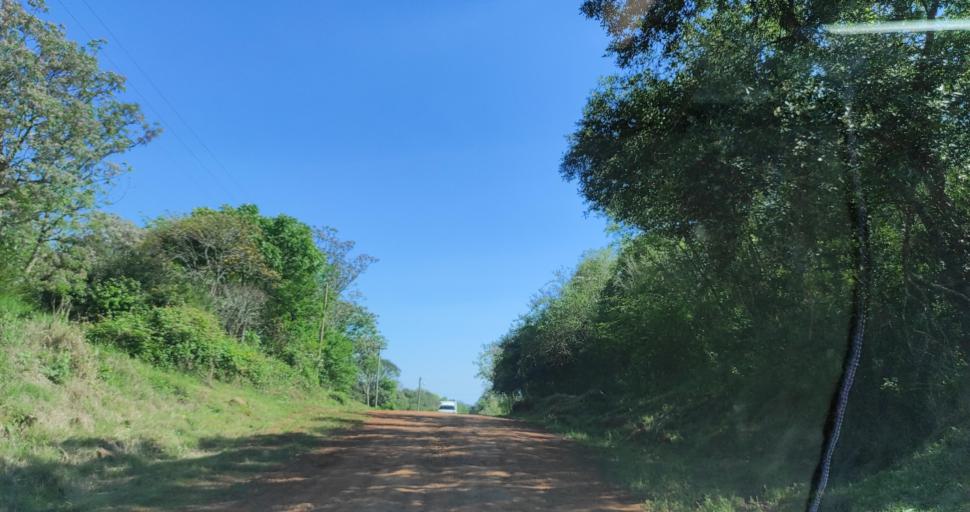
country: AR
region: Misiones
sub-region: Departamento de Candelaria
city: Loreto
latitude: -27.3195
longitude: -55.5321
